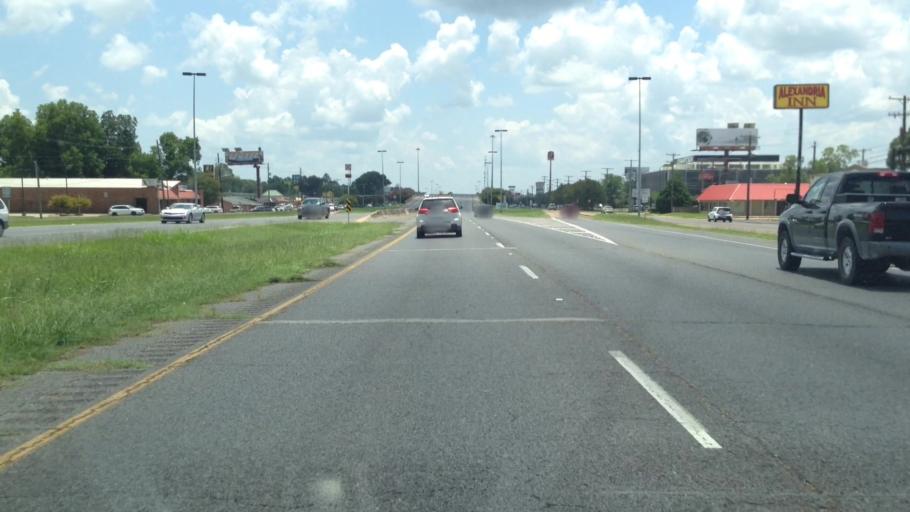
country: US
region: Louisiana
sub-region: Rapides Parish
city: Alexandria
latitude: 31.2903
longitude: -92.4766
